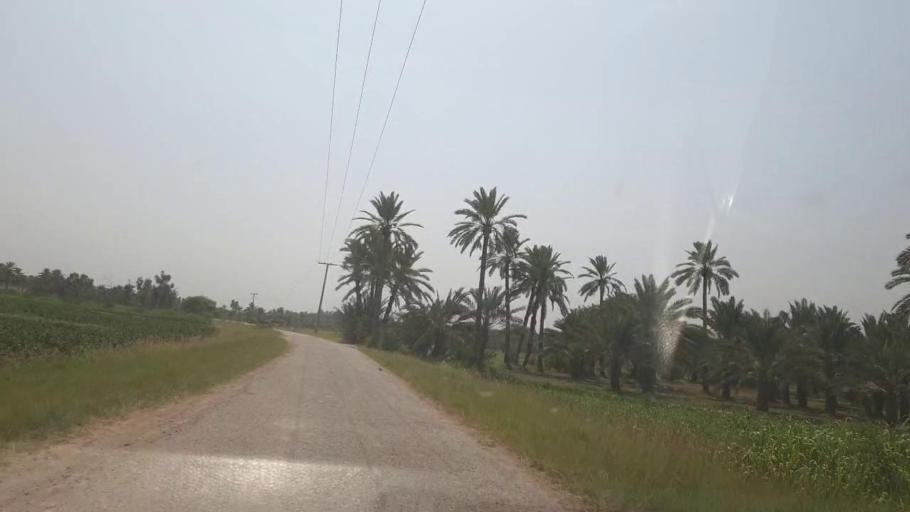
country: PK
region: Sindh
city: Khairpur
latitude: 27.4694
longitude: 68.7529
